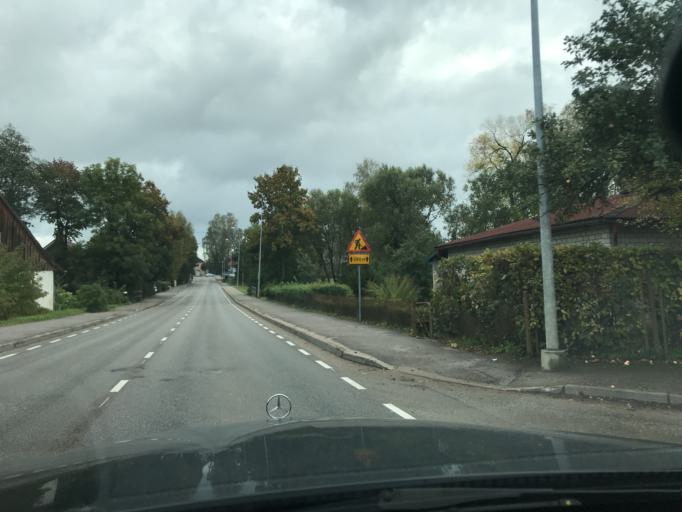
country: EE
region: Valgamaa
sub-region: Torva linn
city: Torva
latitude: 58.0050
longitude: 25.9196
